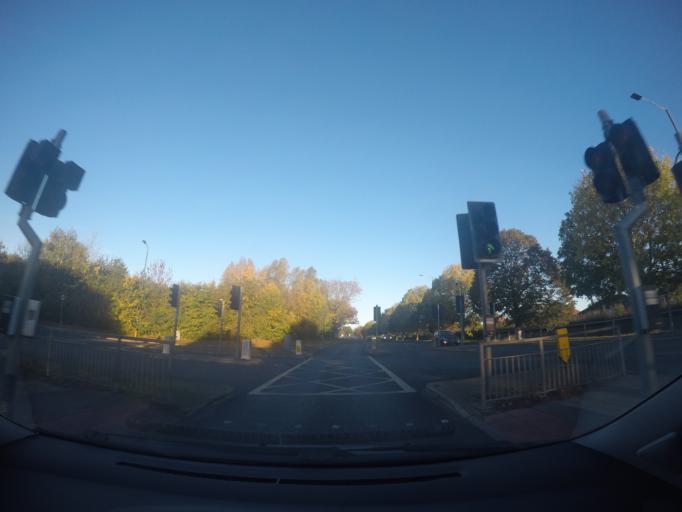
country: GB
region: England
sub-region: City of York
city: Skelton
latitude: 53.9846
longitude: -1.1201
